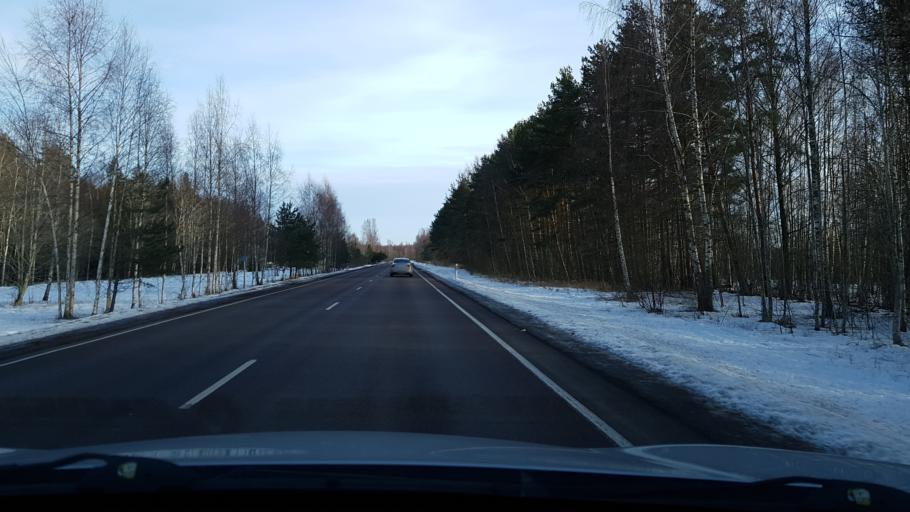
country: EE
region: Tartu
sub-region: Puhja vald
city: Puhja
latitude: 58.3984
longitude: 26.1085
